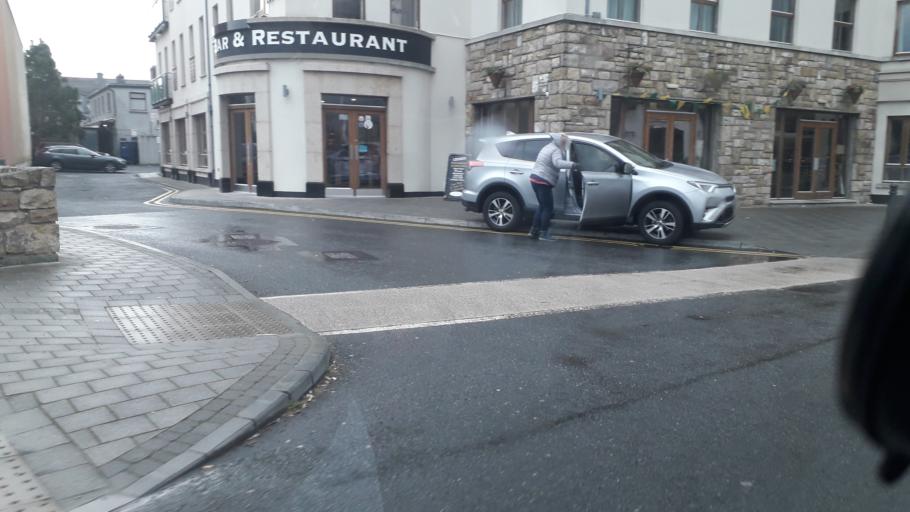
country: IE
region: Connaught
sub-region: County Leitrim
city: Carrick-on-Shannon
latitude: 53.9433
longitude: -8.0937
